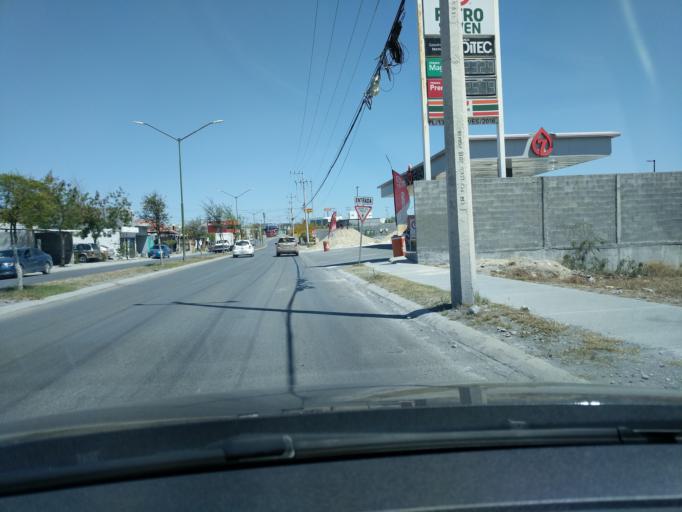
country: MX
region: Nuevo Leon
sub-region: Pesqueria
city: Colinas del Aeropuerto
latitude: 25.8155
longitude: -100.1089
